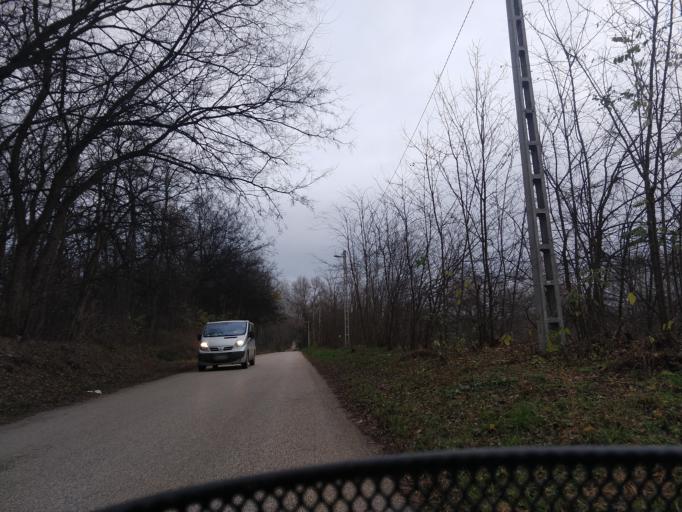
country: HU
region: Pest
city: Erdokertes
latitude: 47.6665
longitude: 19.2921
